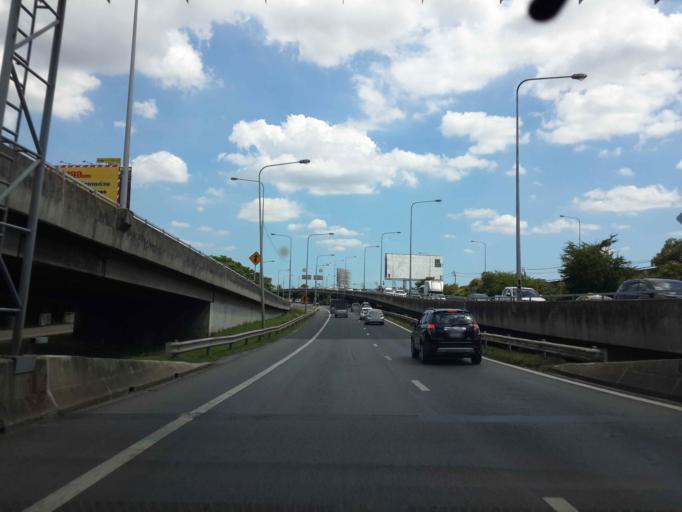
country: TH
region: Bangkok
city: Chom Thong
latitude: 13.6803
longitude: 100.4772
